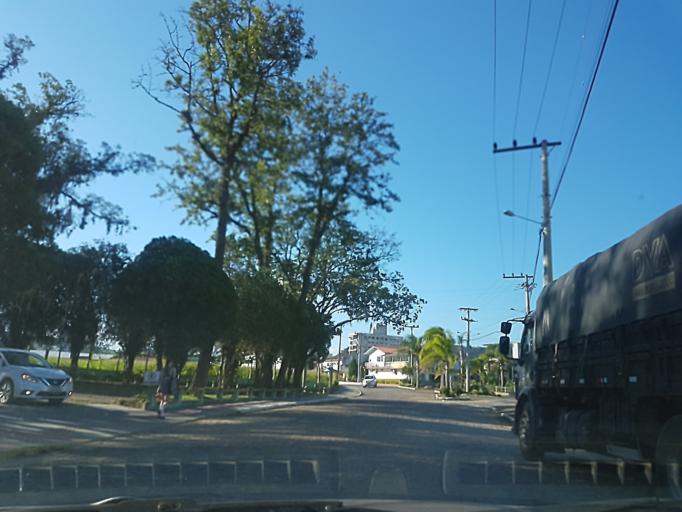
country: BR
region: Santa Catarina
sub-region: Braco Do Norte
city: Braco do Norte
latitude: -28.3281
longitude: -49.1737
